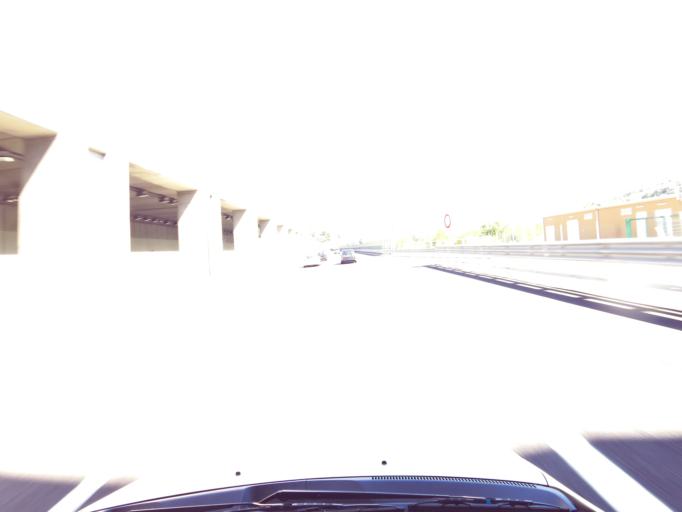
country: IT
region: Emilia-Romagna
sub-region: Provincia di Bologna
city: Grizzana
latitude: 44.2751
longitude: 11.1949
